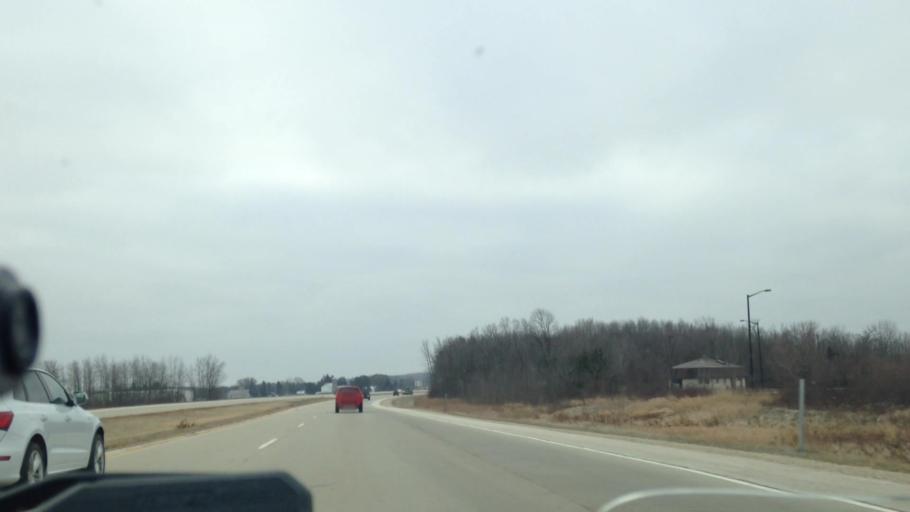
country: US
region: Wisconsin
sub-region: Washington County
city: Jackson
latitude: 43.3198
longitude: -88.1855
